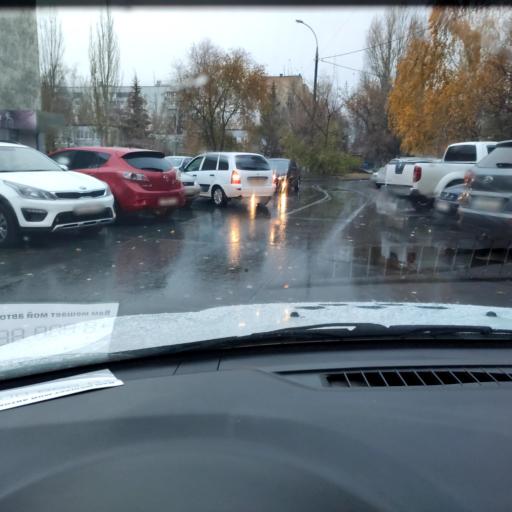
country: RU
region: Samara
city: Tol'yatti
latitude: 53.5079
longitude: 49.4475
